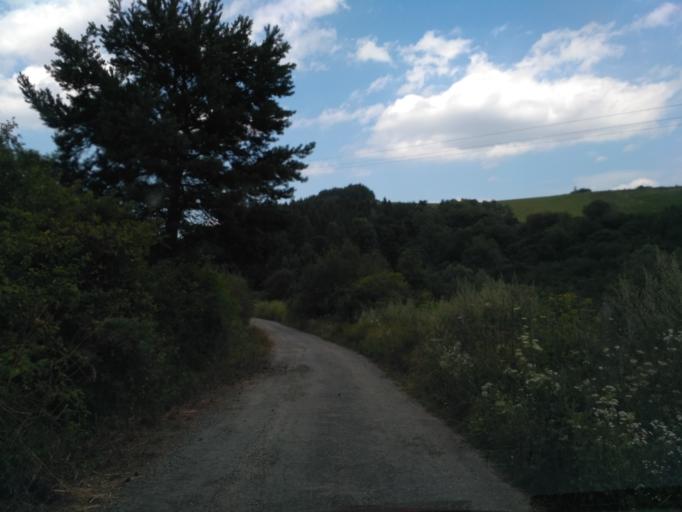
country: SK
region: Presovsky
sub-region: Okres Presov
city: Presov
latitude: 48.9129
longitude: 21.1803
